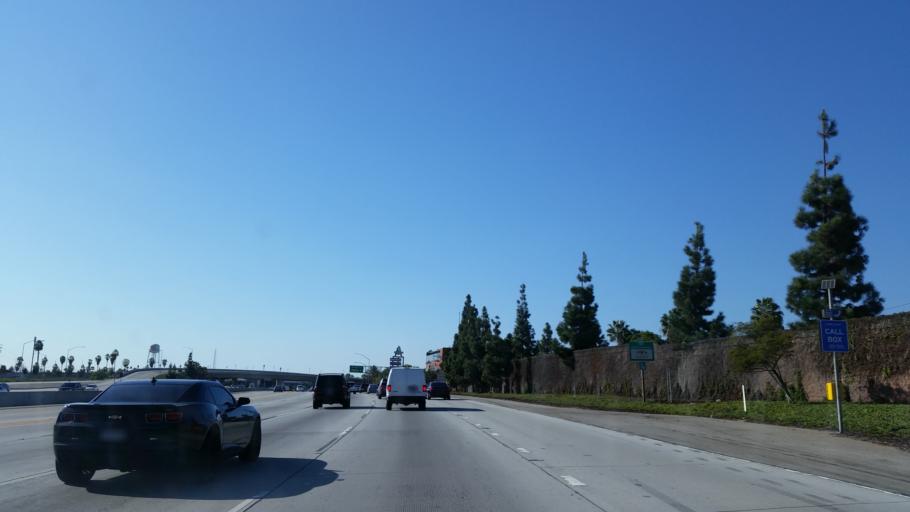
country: US
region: California
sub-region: Orange County
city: Anaheim
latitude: 33.8340
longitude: -117.9346
